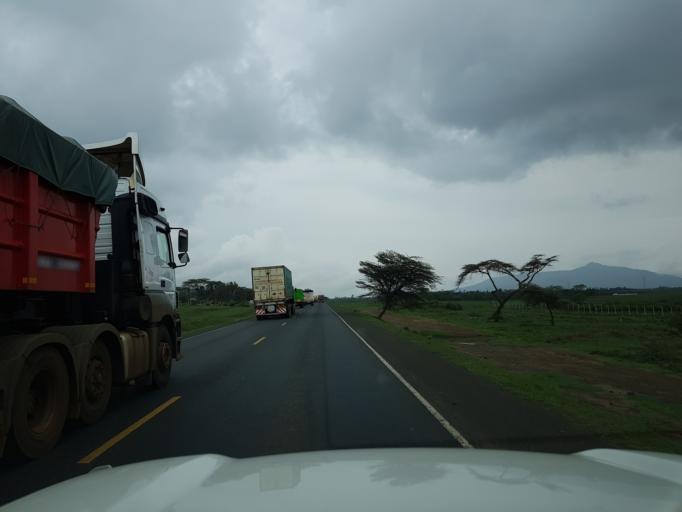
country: KE
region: Nakuru
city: Naivasha
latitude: -0.8132
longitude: 36.4661
